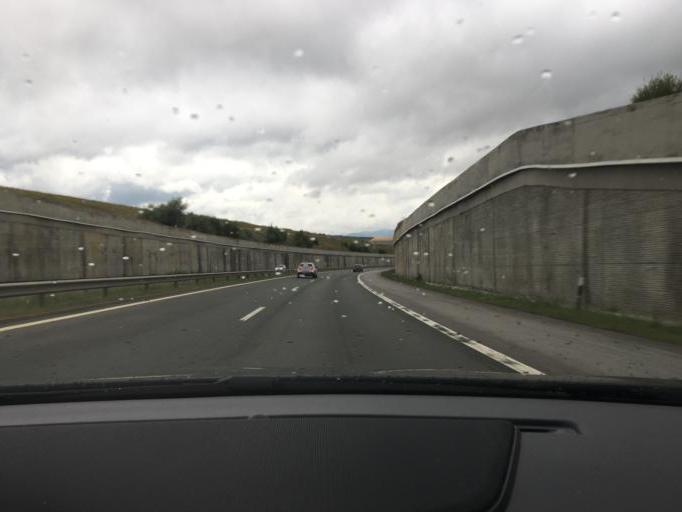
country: BG
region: Pernik
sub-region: Obshtina Pernik
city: Pernik
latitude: 42.6172
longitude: 23.1397
